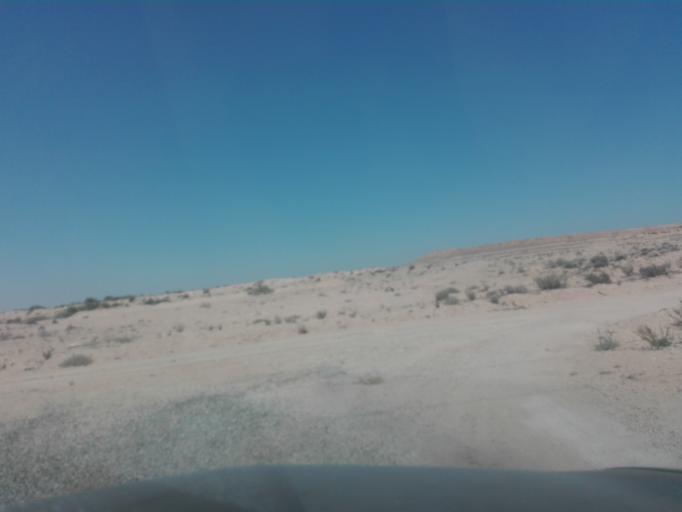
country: TN
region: Qabis
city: Gabes
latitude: 33.8439
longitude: 9.9816
